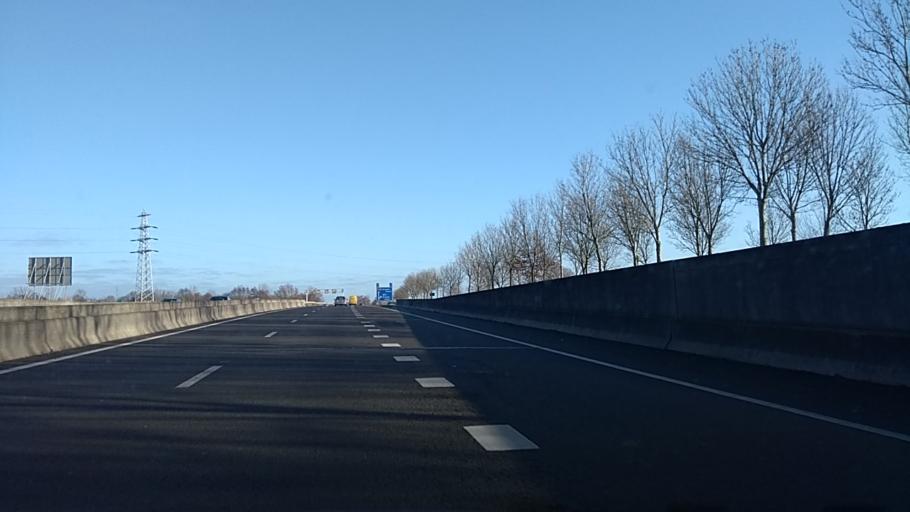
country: NL
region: Drenthe
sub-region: Gemeente Meppel
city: Meppel
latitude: 52.6816
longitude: 6.1970
